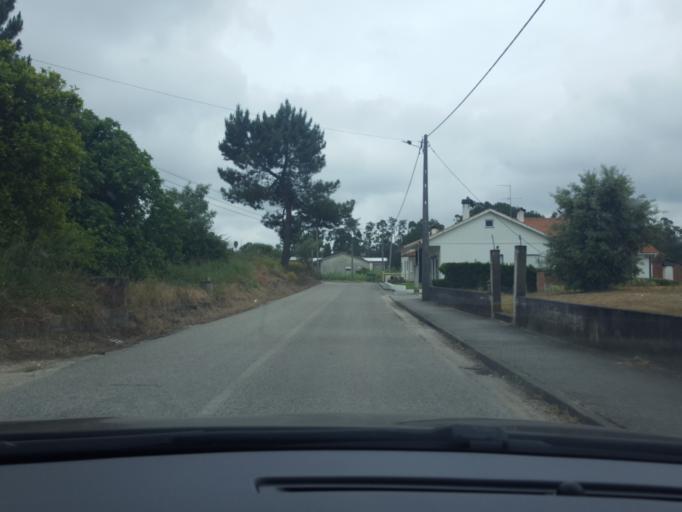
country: PT
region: Leiria
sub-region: Leiria
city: Caranguejeira
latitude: 39.7932
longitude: -8.7515
